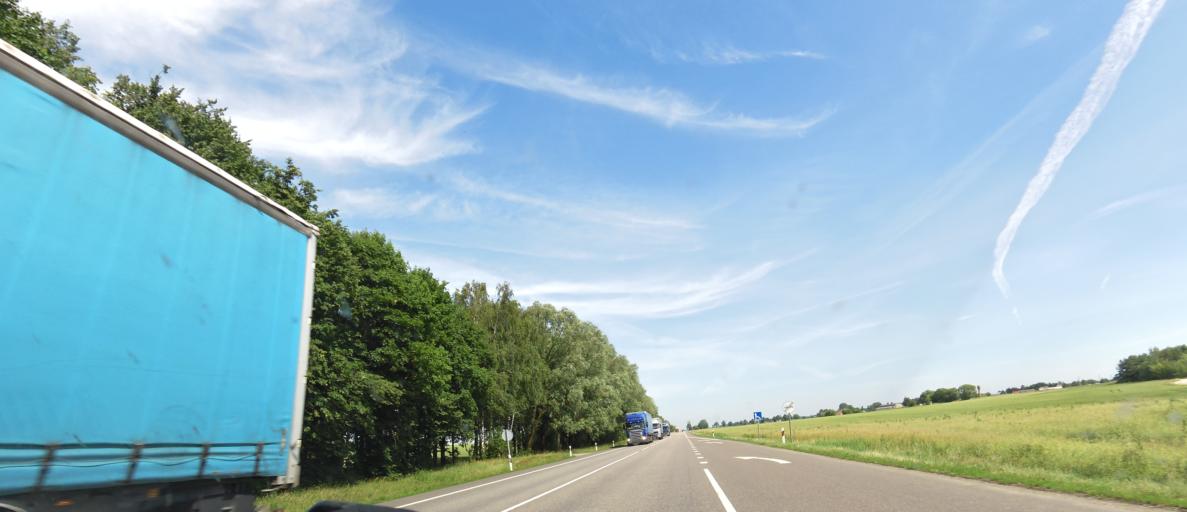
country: LT
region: Panevezys
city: Pasvalys
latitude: 55.9683
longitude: 24.3405
